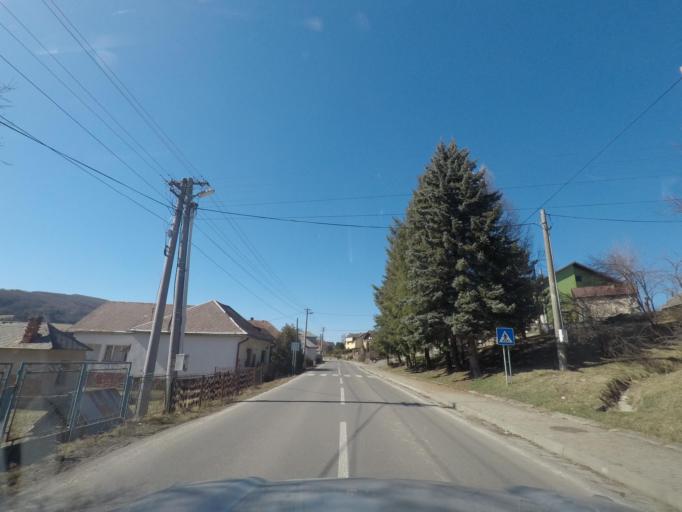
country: UA
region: Zakarpattia
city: Velykyi Bereznyi
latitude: 48.8988
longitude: 22.3956
